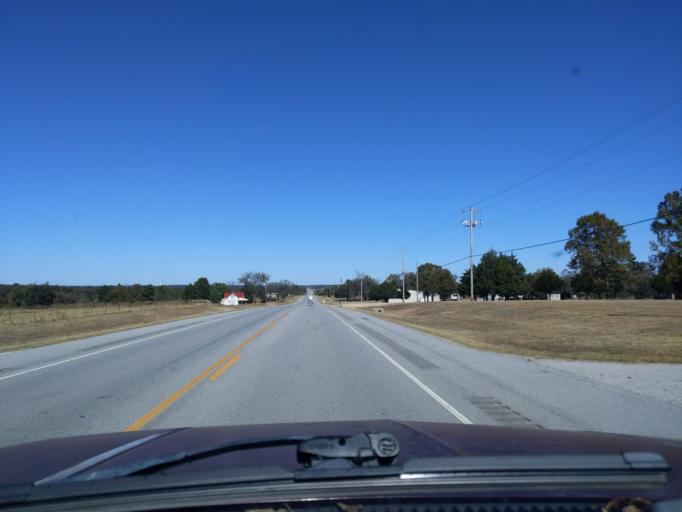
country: US
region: Oklahoma
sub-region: Creek County
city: Bristow
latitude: 35.7854
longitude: -96.3872
